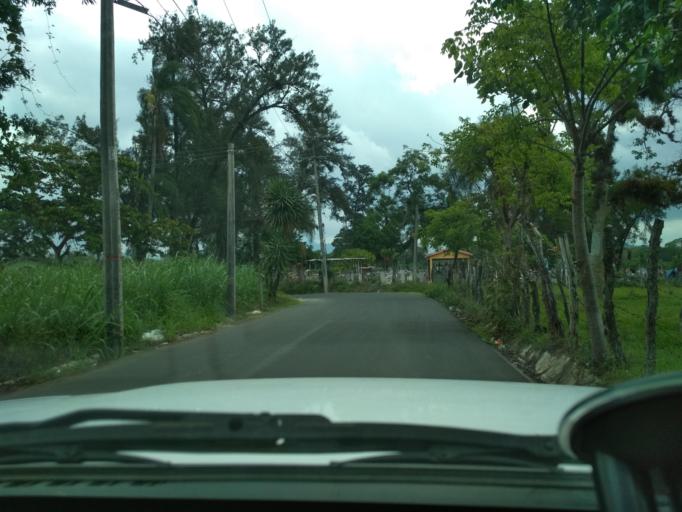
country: MX
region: Veracruz
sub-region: Cordoba
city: San Jose de Abajo [Unidad Habitacional]
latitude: 18.9234
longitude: -96.9608
